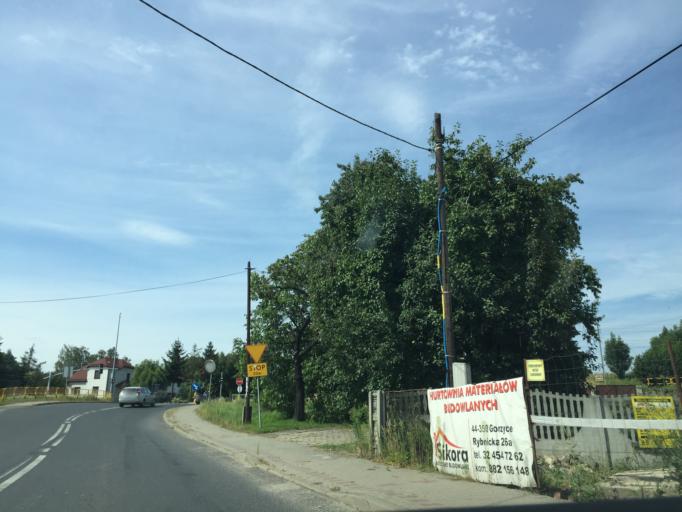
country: PL
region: Silesian Voivodeship
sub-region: Powiat wodzislawski
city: Gorzyce
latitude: 49.9586
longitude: 18.3991
